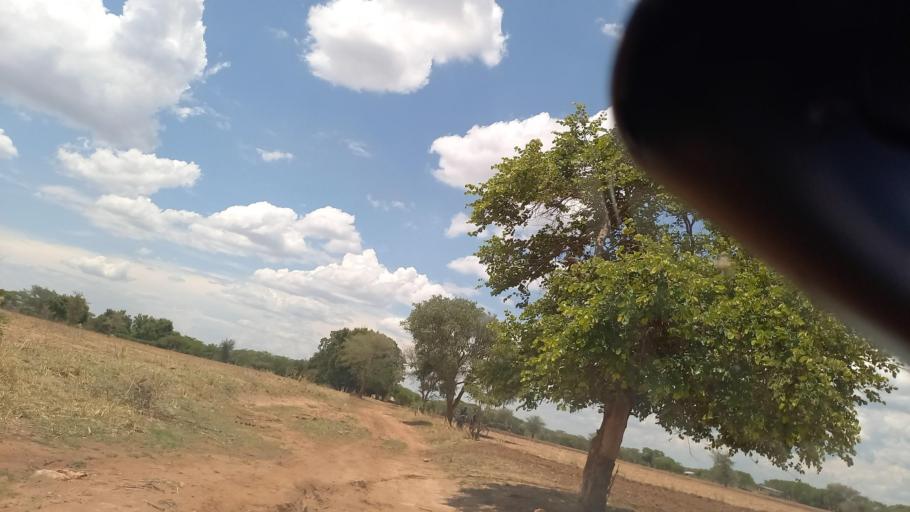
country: ZM
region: Southern
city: Mazabuka
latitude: -16.1126
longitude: 27.8147
